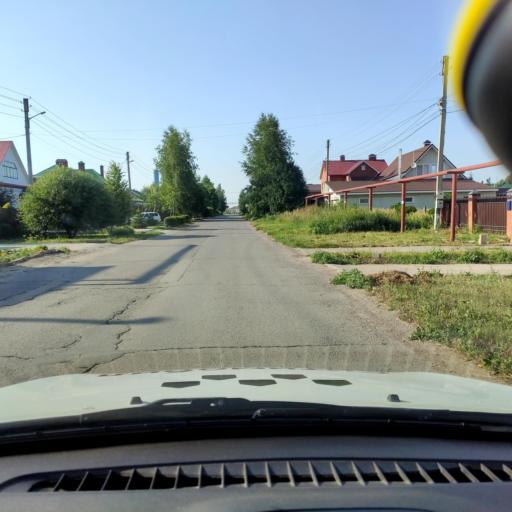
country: RU
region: Samara
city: Podstepki
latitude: 53.5190
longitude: 49.1808
